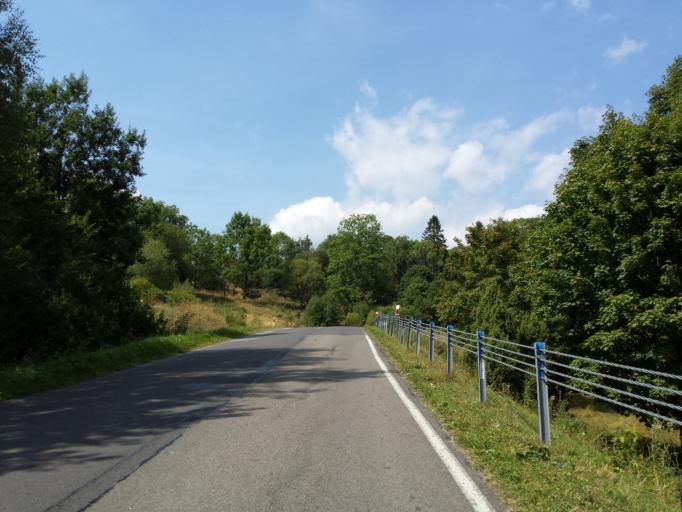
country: PL
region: Subcarpathian Voivodeship
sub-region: Powiat bieszczadzki
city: Lutowiska
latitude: 49.1408
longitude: 22.5518
